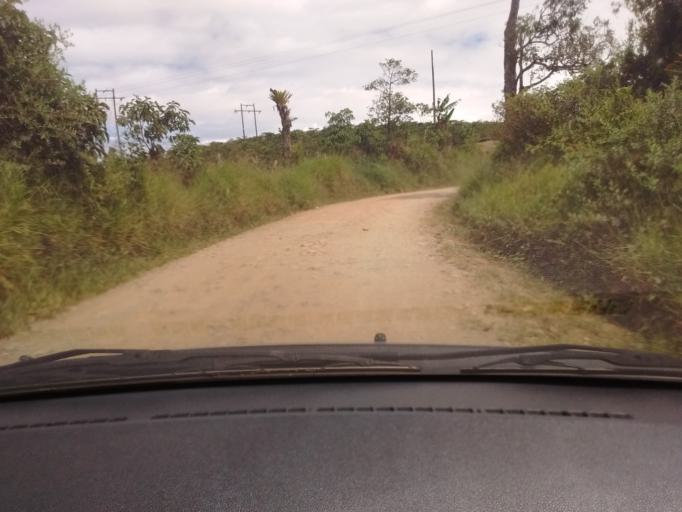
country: CO
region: Cauca
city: El Tambo
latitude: 2.4461
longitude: -76.8208
